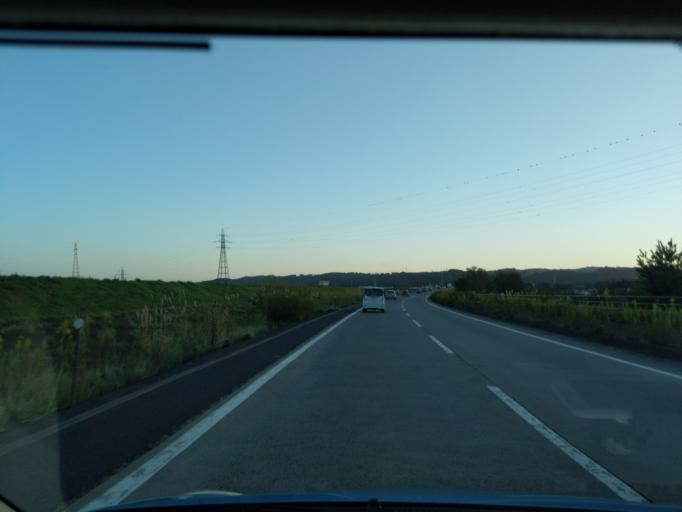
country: JP
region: Iwate
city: Ichinoseki
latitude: 38.9834
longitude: 141.1233
